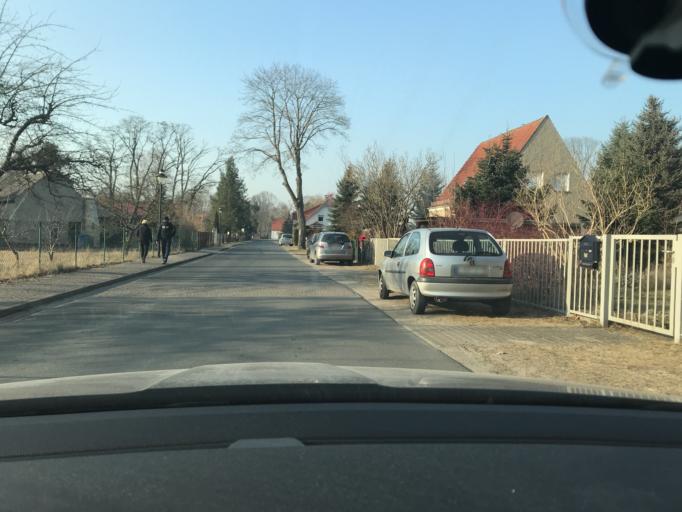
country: DE
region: Brandenburg
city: Munchehofe
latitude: 52.2218
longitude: 13.7733
